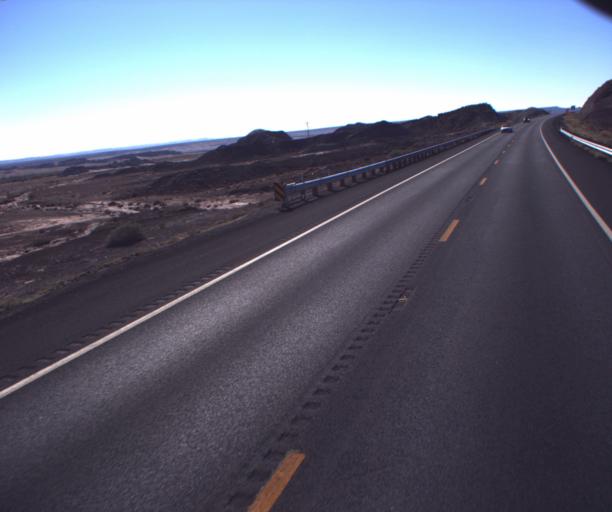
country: US
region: Arizona
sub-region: Coconino County
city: Tuba City
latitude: 36.0856
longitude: -111.3922
